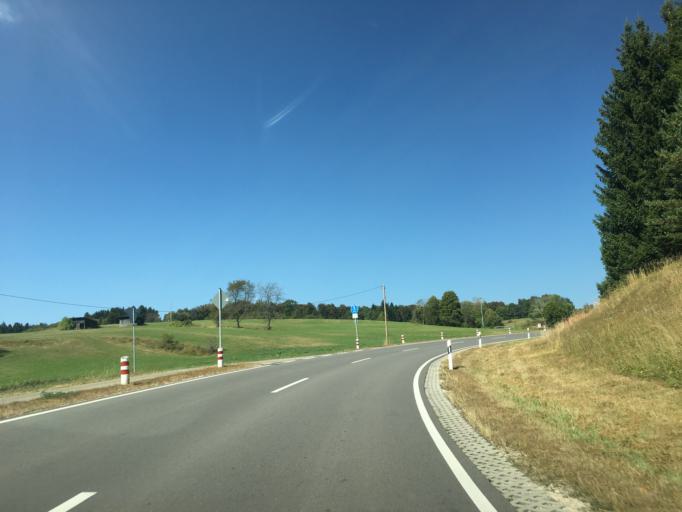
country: DE
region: Baden-Wuerttemberg
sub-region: Tuebingen Region
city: Munsingen
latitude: 48.3844
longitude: 9.4854
